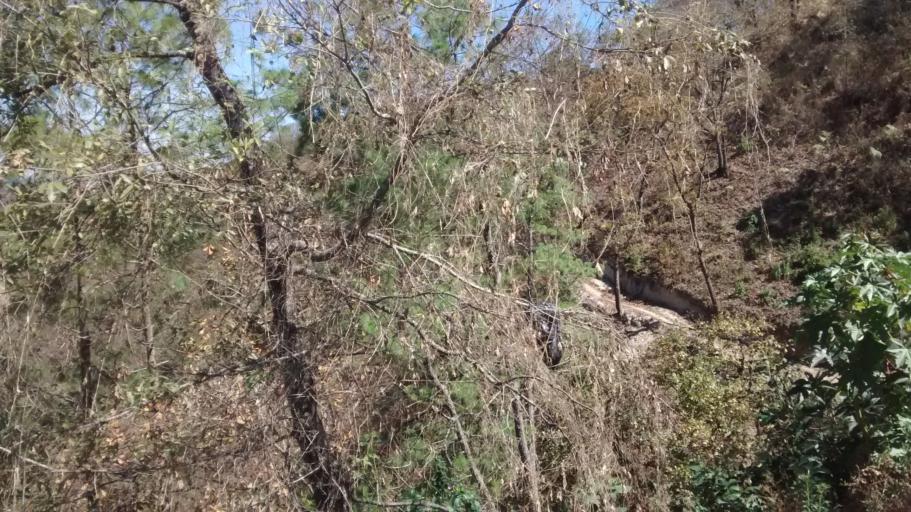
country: GT
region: Sacatepequez
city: Santo Domingo Xenacoj
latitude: 14.6854
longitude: -90.7283
